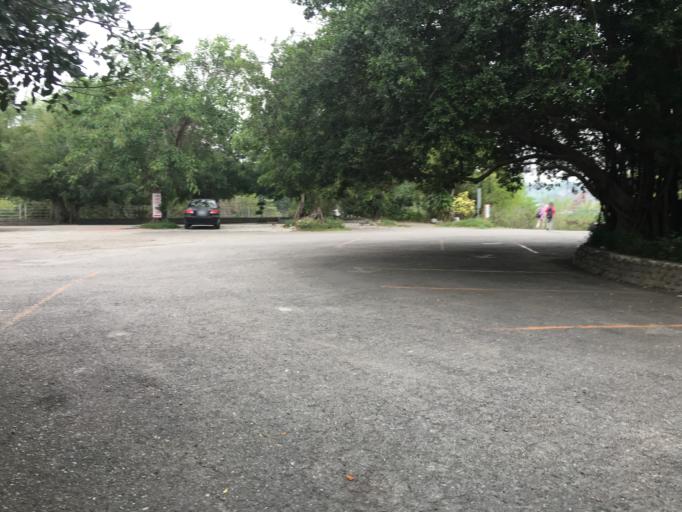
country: TW
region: Taiwan
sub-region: Tainan
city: Tainan
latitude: 22.8865
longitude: 120.3892
